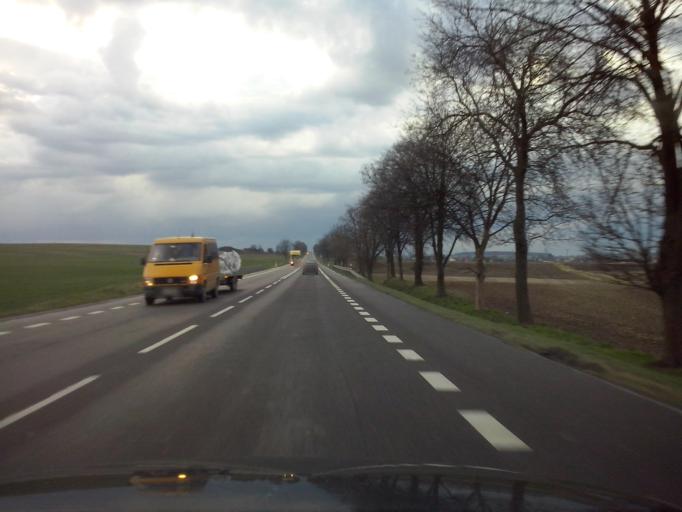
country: PL
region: Lublin Voivodeship
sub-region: Chelm
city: Chelm
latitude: 51.1661
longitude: 23.3737
